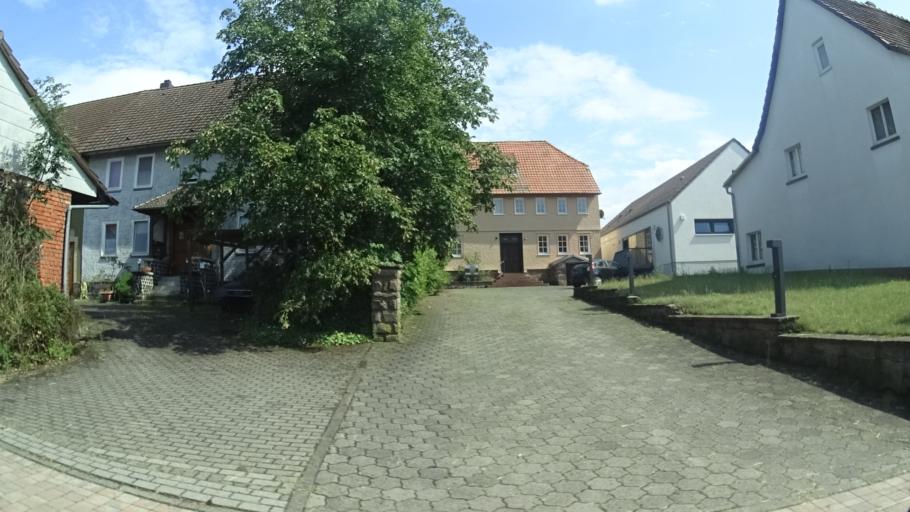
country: DE
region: Hesse
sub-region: Regierungsbezirk Giessen
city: Lauterbach
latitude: 50.6618
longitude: 9.3890
